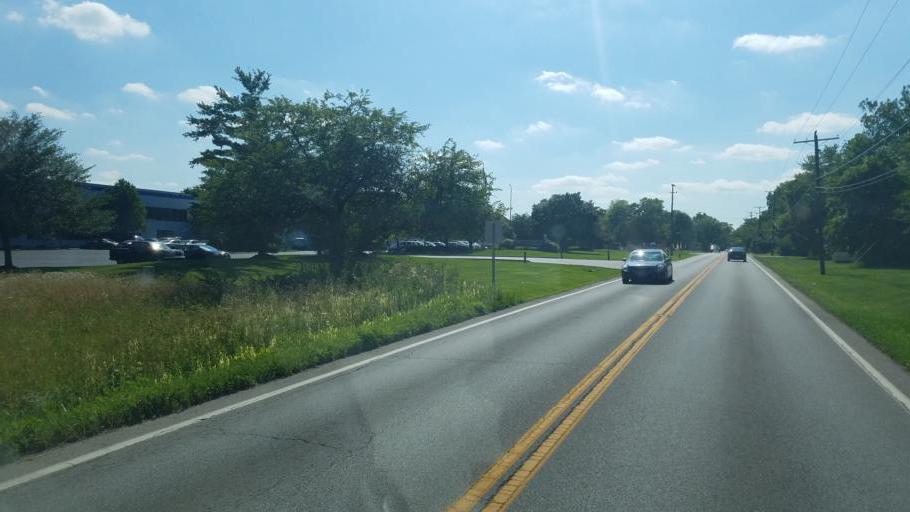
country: US
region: Ohio
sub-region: Franklin County
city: Worthington
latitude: 40.0905
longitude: -83.0608
